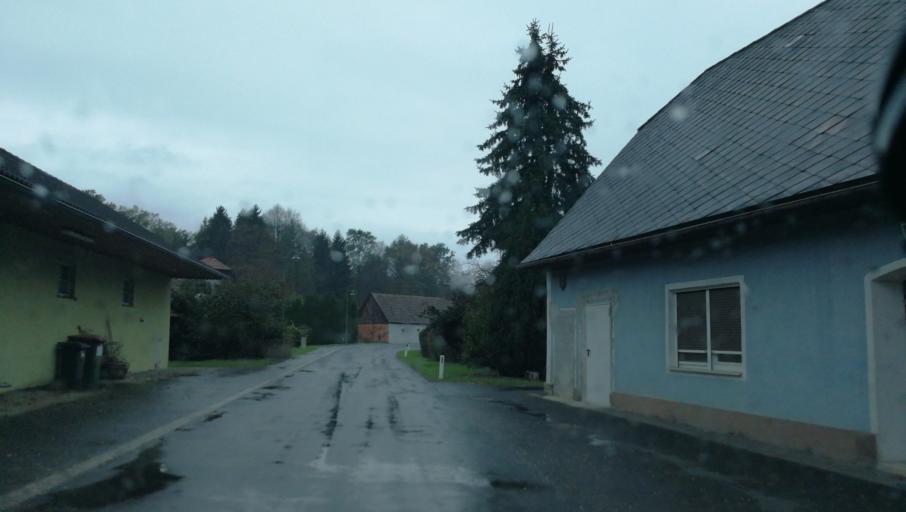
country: AT
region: Styria
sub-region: Politischer Bezirk Leibnitz
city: Spielfeld
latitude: 46.7329
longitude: 15.6618
